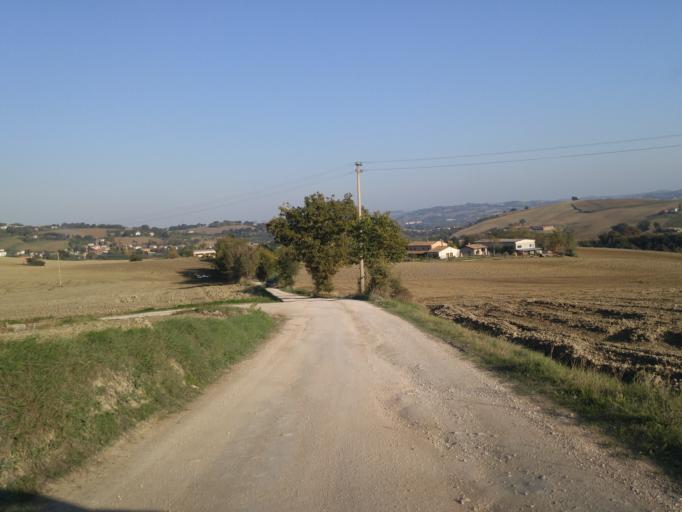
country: IT
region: The Marches
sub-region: Provincia di Pesaro e Urbino
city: Montefelcino
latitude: 43.7183
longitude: 12.8191
